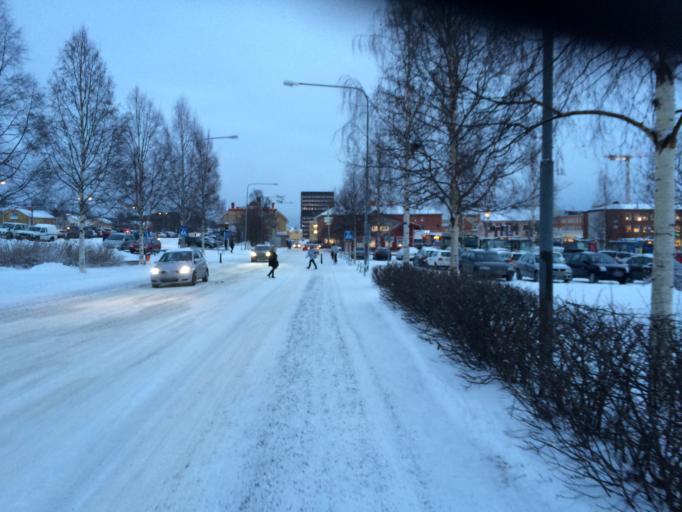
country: SE
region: Vaesterbotten
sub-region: Skelleftea Kommun
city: Skelleftea
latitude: 64.7532
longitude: 20.9523
